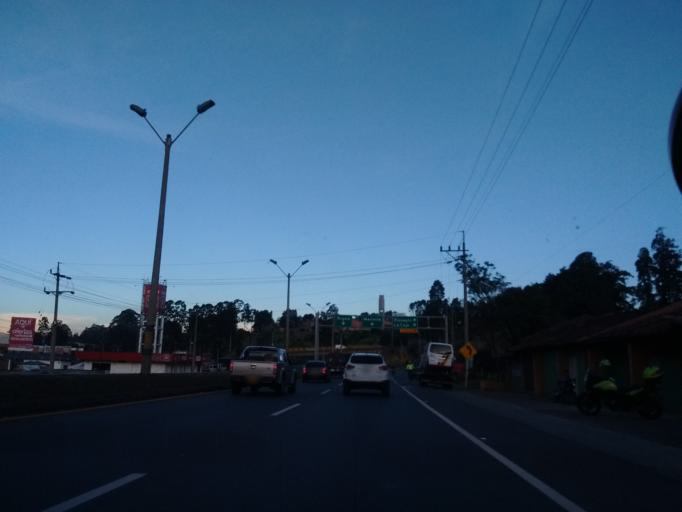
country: CO
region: Antioquia
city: Rionegro
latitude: 6.1803
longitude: -75.3691
